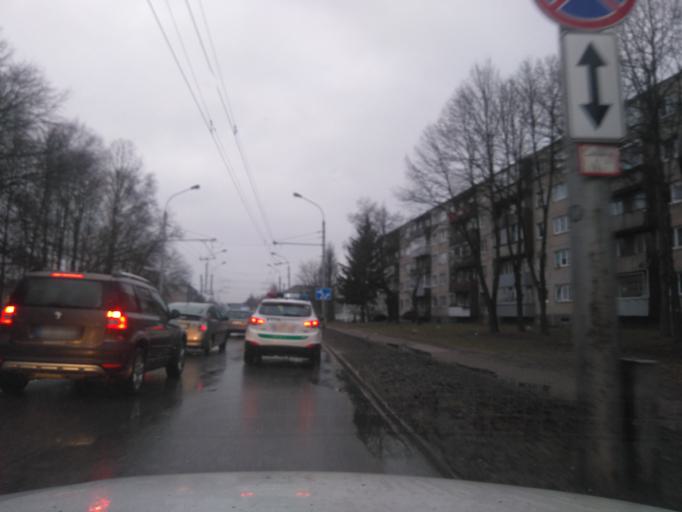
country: LT
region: Kauno apskritis
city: Dainava (Kaunas)
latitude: 54.9179
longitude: 23.9722
